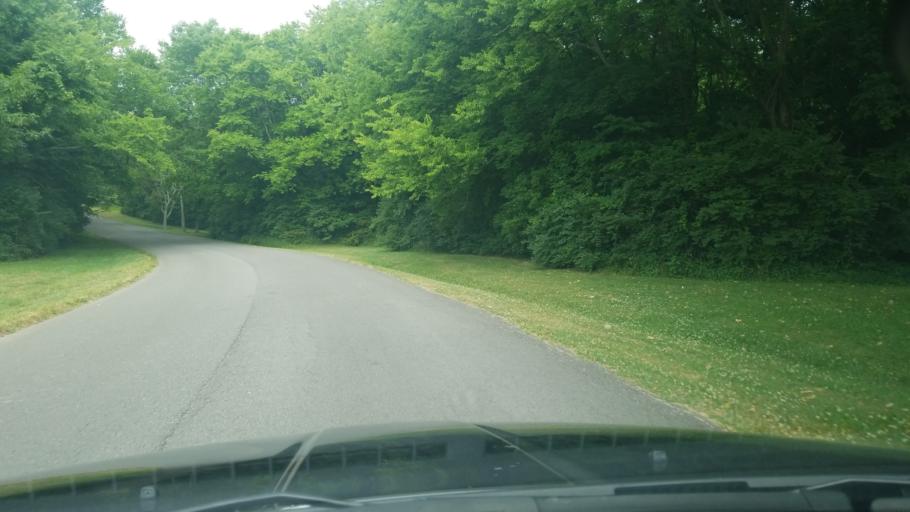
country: US
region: Tennessee
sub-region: Davidson County
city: Goodlettsville
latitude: 36.2753
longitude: -86.7463
